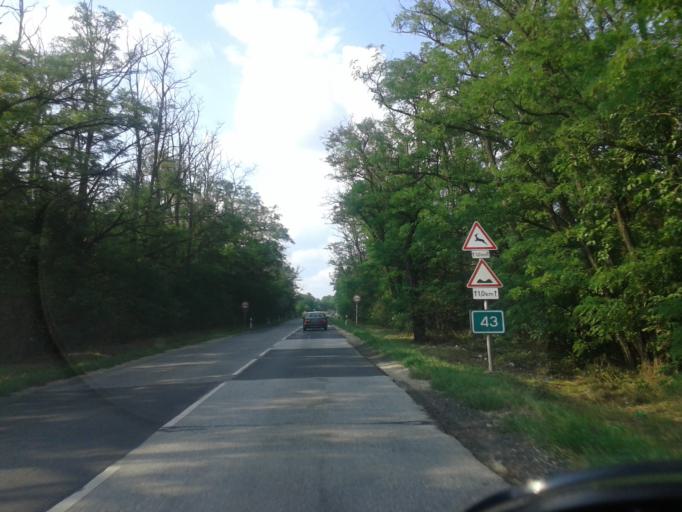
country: HU
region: Pest
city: Kiskunlachaza
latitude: 47.1561
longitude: 18.9987
